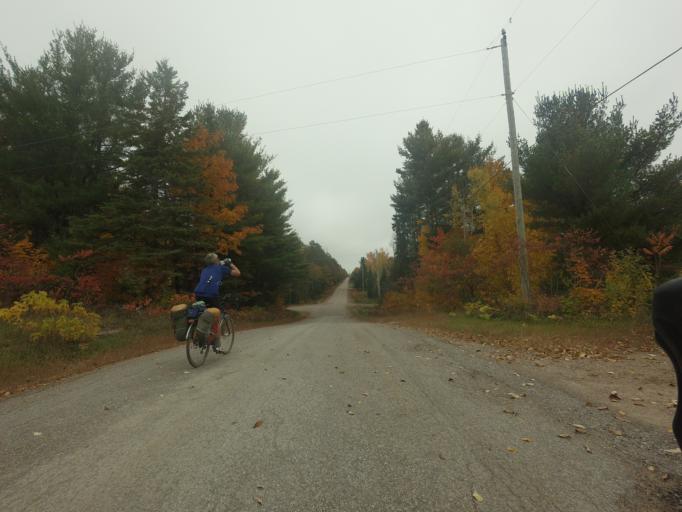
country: CA
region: Ontario
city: Petawawa
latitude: 45.7541
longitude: -77.2603
